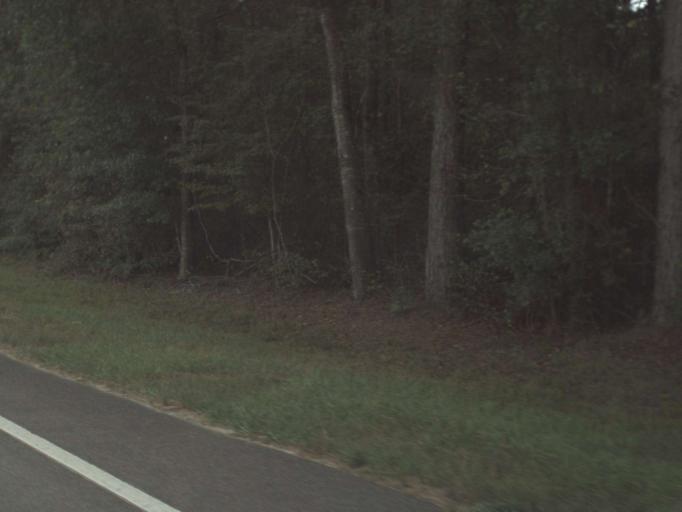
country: US
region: Florida
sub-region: Walton County
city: DeFuniak Springs
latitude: 30.6922
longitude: -85.9364
